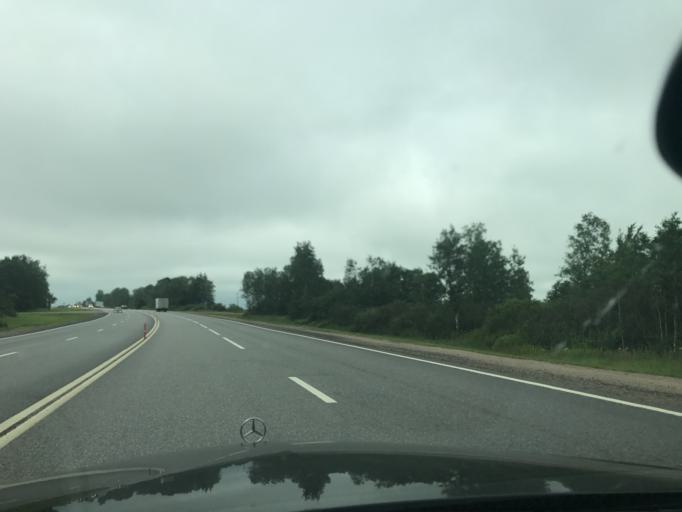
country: RU
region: Smolensk
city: Pechersk
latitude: 54.8605
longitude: 31.9003
